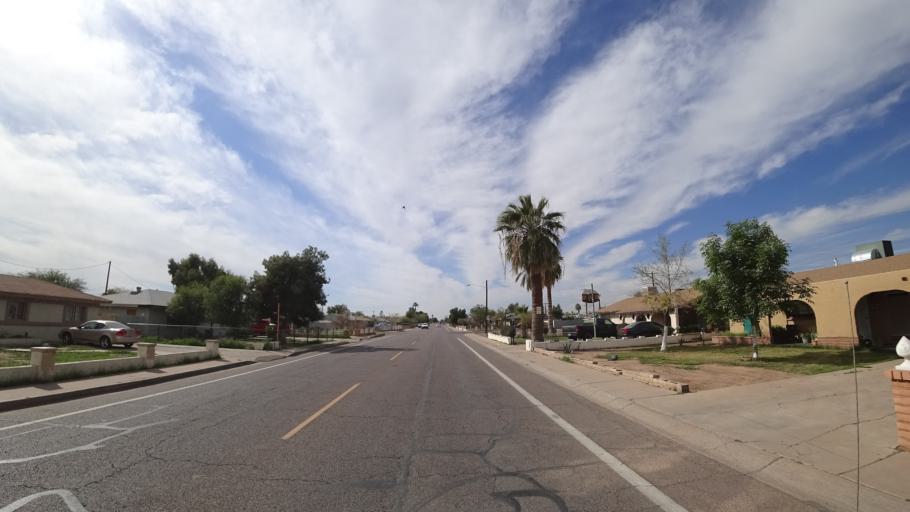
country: US
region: Arizona
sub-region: Maricopa County
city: Phoenix
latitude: 33.4732
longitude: -112.1379
